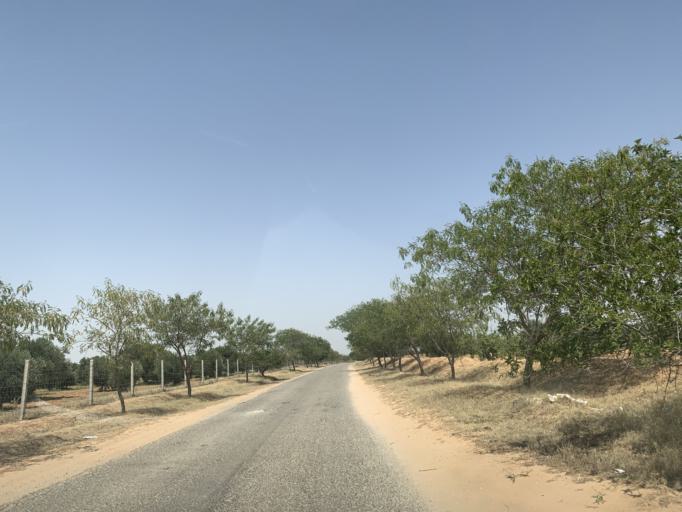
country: TN
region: Al Mahdiyah
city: Shurban
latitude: 35.1921
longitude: 10.2498
